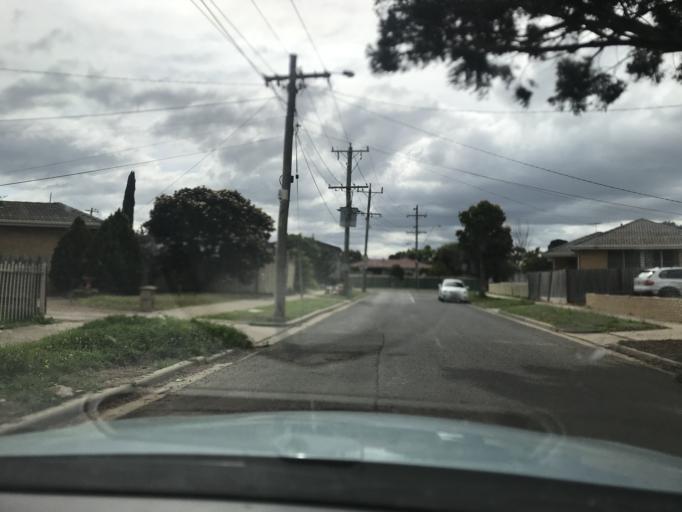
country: AU
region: Victoria
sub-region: Hobsons Bay
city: Laverton
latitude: -37.8556
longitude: 144.7747
